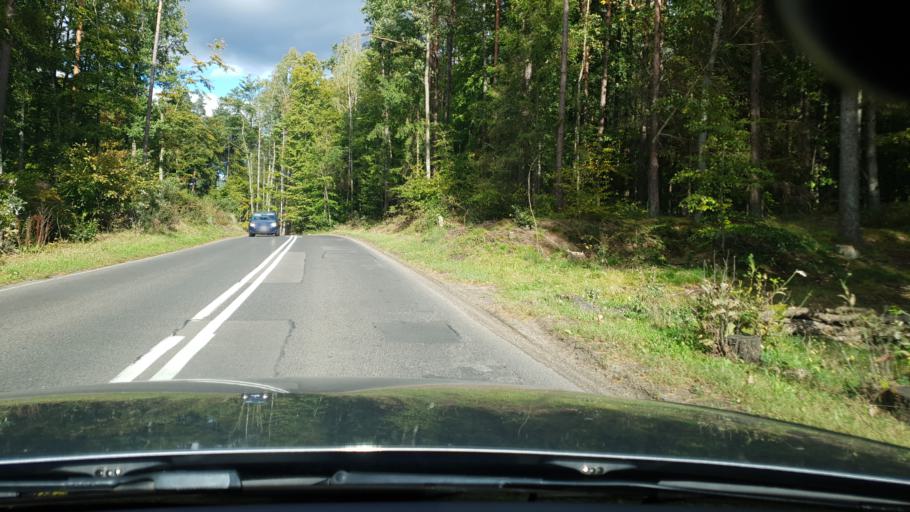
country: PL
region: Pomeranian Voivodeship
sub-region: Powiat wejherowski
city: Koleczkowo
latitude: 54.5045
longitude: 18.3691
